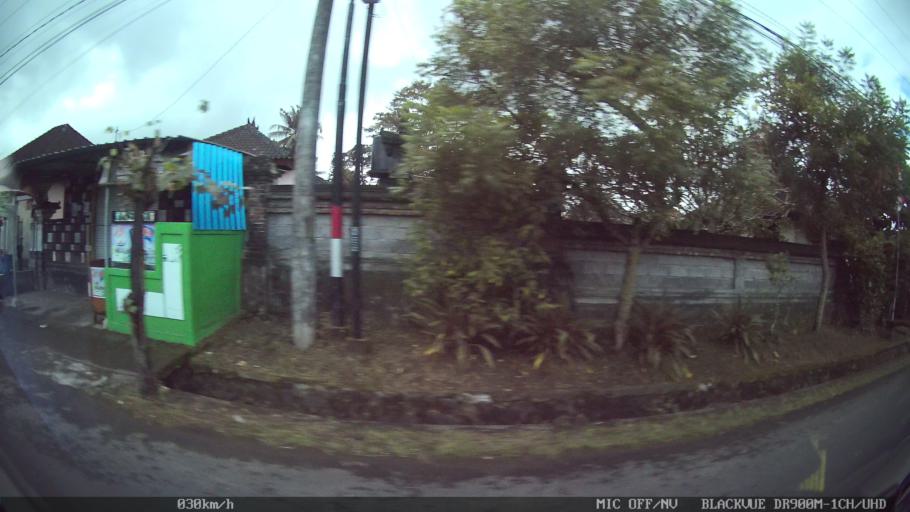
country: ID
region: Bali
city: Banjar Mambalkajanan
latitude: -8.5503
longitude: 115.2121
